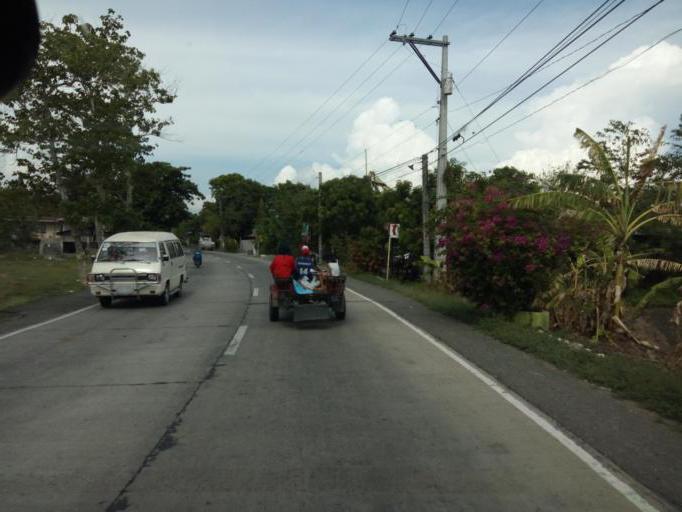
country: PH
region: Ilocos
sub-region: Province of Pangasinan
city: Balungao
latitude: 15.8963
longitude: 120.6833
